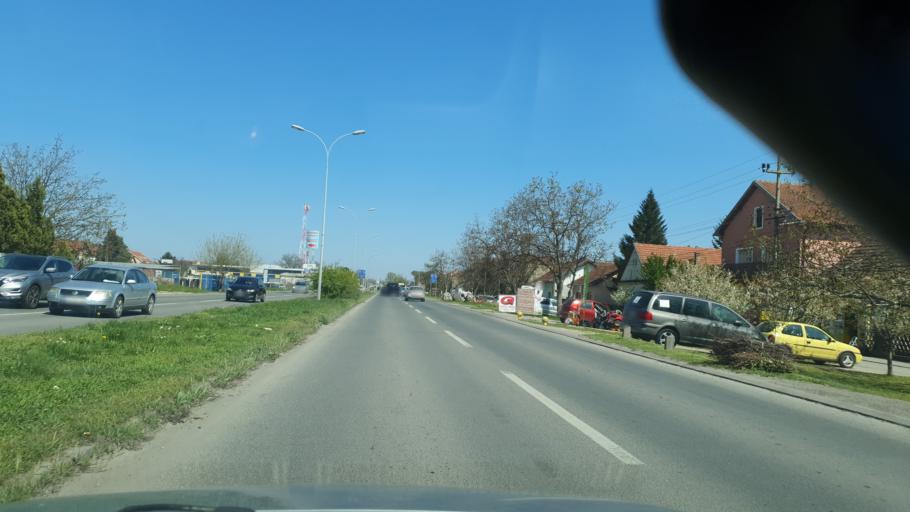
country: RS
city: Veternik
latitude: 45.2480
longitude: 19.7455
